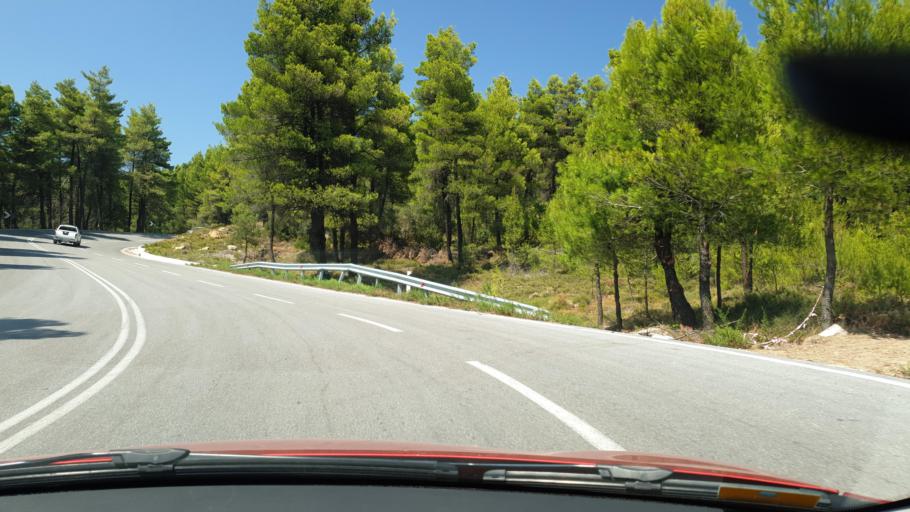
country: GR
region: Central Greece
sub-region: Nomos Evvoias
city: Politika
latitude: 38.6441
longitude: 23.5636
